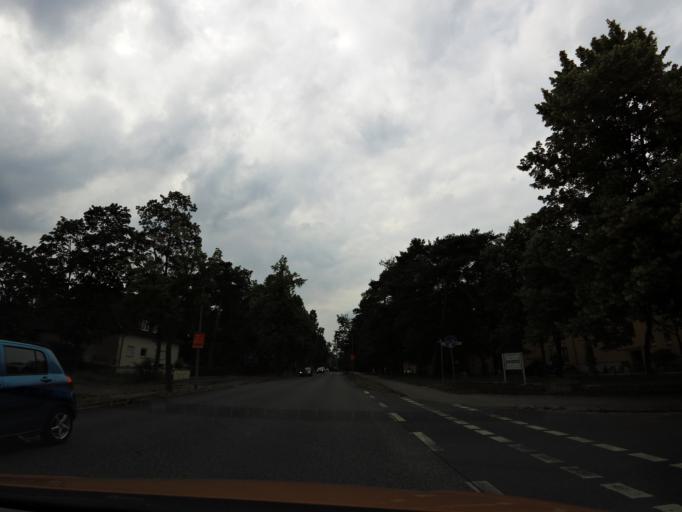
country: DE
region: Brandenburg
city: Zossen
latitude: 52.1650
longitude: 13.4734
